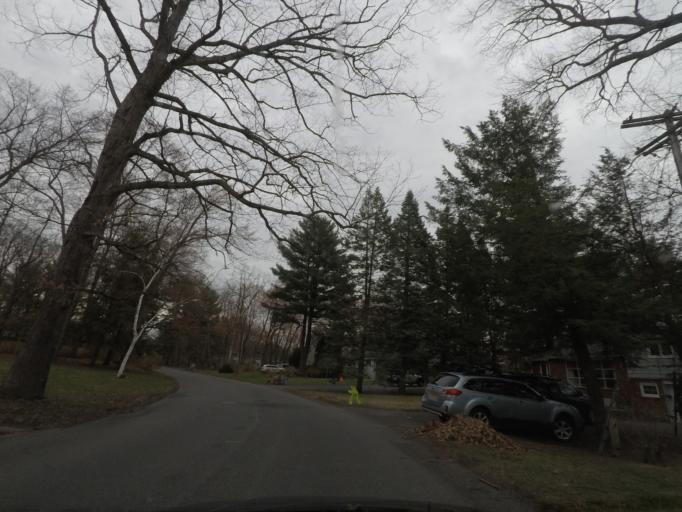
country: US
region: New York
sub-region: Albany County
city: Delmar
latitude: 42.6108
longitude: -73.8439
